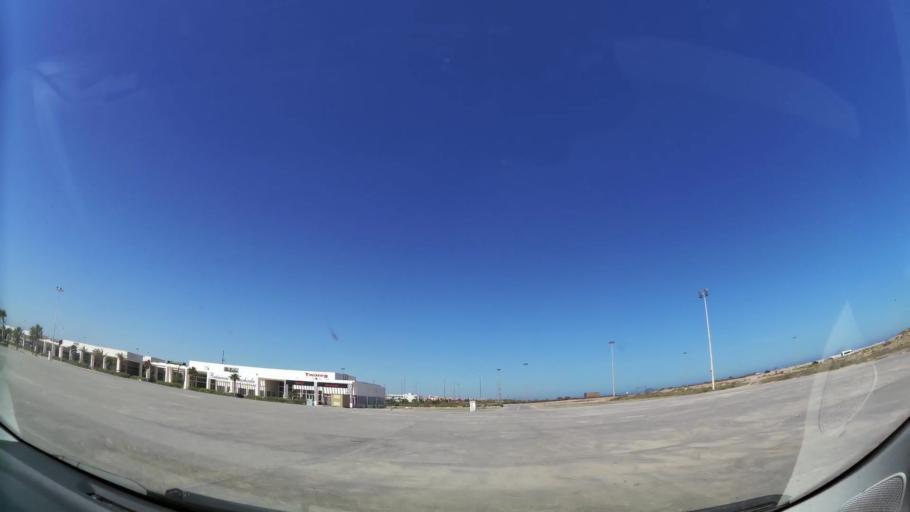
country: MA
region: Oriental
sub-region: Berkane-Taourirt
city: Madagh
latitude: 35.1118
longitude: -2.2969
